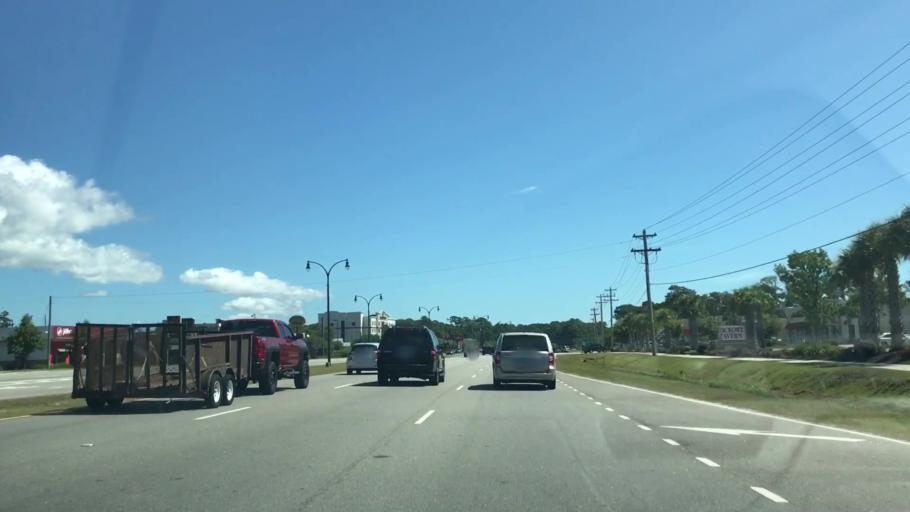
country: US
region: South Carolina
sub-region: Horry County
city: North Myrtle Beach
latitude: 33.8425
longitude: -78.6611
